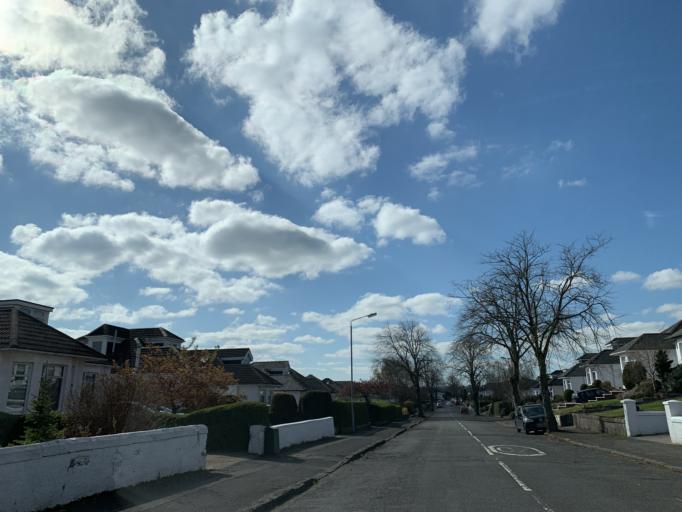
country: GB
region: Scotland
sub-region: East Renfrewshire
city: Clarkston
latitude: 55.7932
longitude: -4.2720
